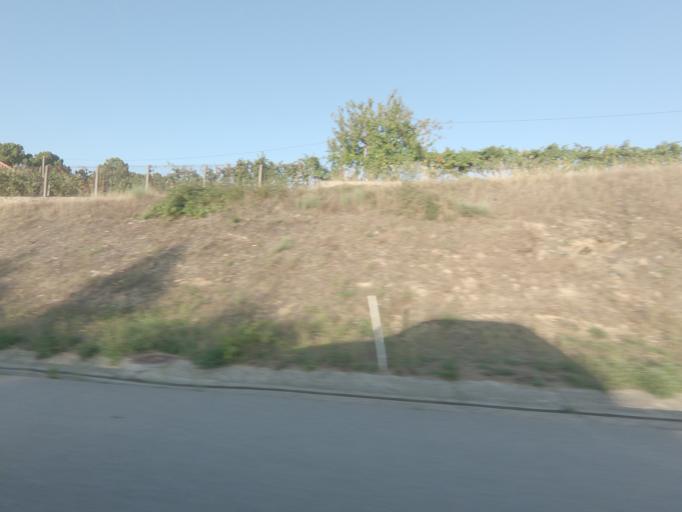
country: PT
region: Vila Real
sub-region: Vila Real
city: Vila Real
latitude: 41.3173
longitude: -7.6952
